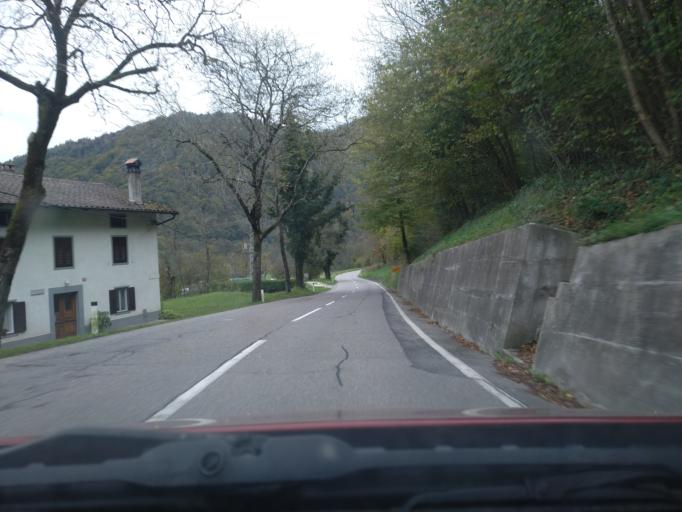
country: SI
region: Tolmin
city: Tolmin
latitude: 46.1618
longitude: 13.7113
